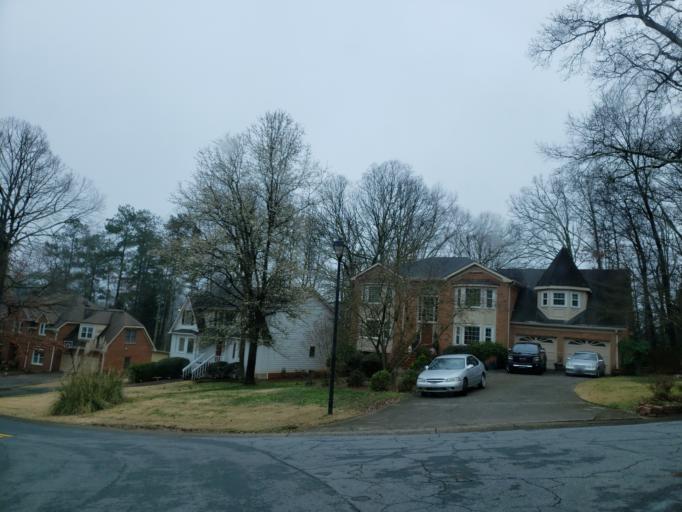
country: US
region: Georgia
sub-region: Cobb County
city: Marietta
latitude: 33.9305
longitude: -84.5754
